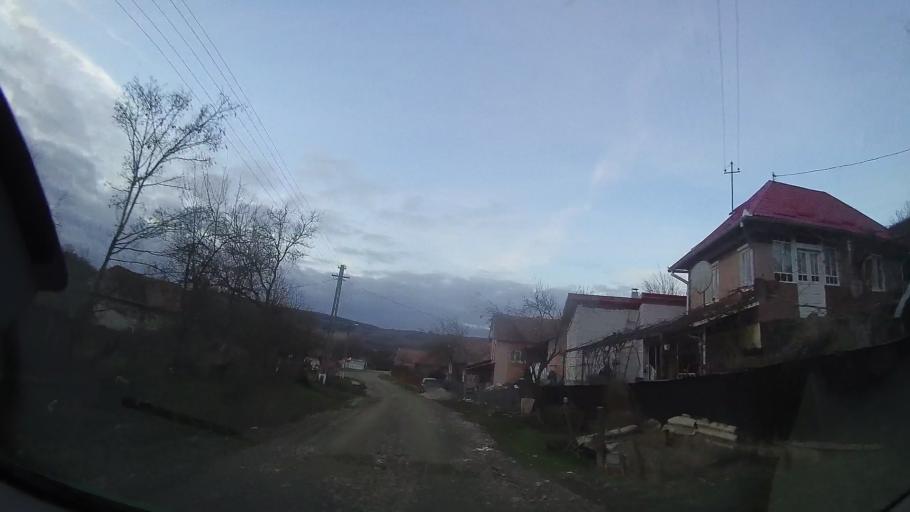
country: RO
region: Cluj
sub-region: Comuna Palatca
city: Palatca
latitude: 46.8651
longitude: 24.0179
